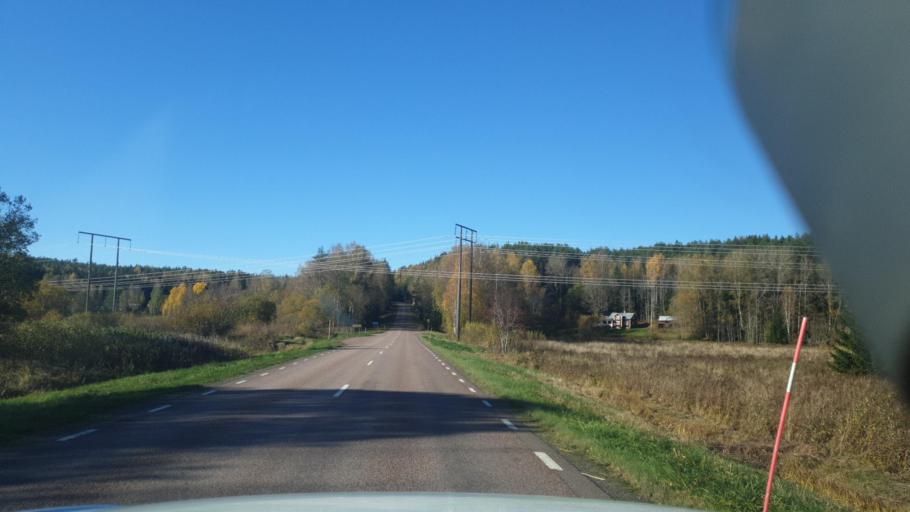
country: SE
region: Vaermland
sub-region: Grums Kommun
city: Grums
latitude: 59.4009
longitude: 13.0611
